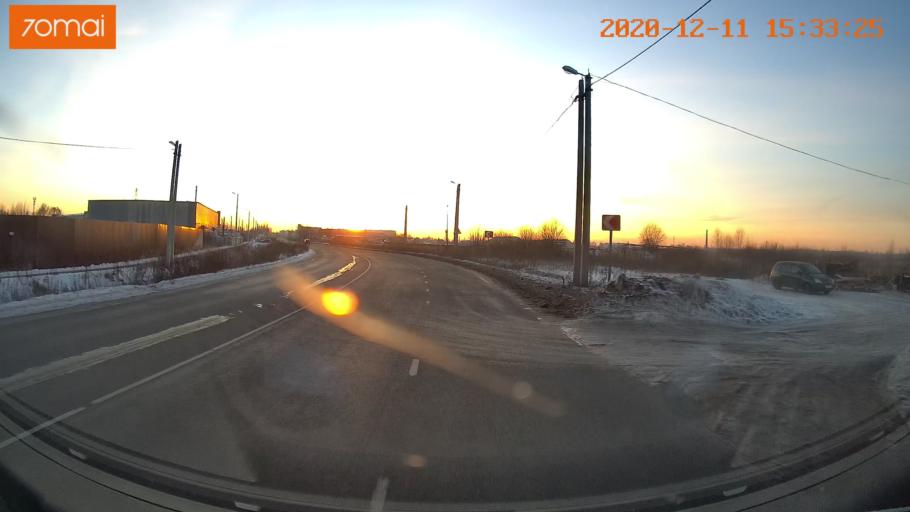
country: RU
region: Ivanovo
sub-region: Gorod Ivanovo
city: Ivanovo
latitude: 57.0529
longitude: 40.9514
